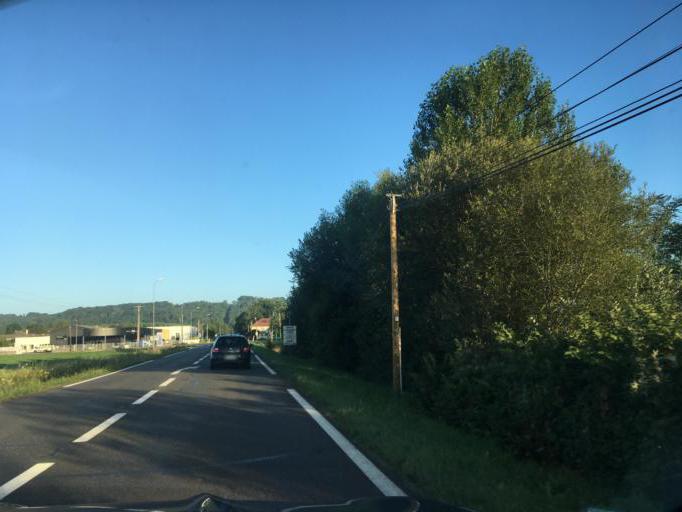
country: FR
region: Midi-Pyrenees
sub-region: Departement des Hautes-Pyrenees
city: Ibos
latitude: 43.2425
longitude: -0.0019
